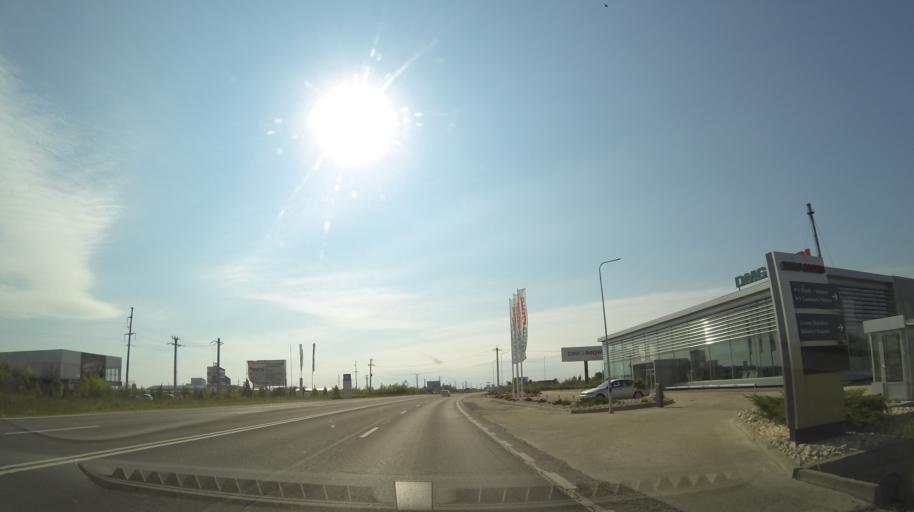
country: RO
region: Arges
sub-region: Comuna Bradu
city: Geamana
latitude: 44.8227
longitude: 24.9257
